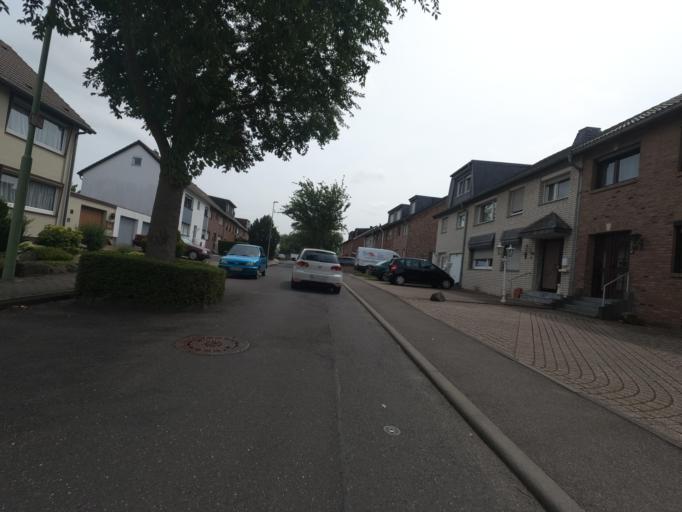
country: DE
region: North Rhine-Westphalia
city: Baesweiler
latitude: 50.9039
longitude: 6.1699
